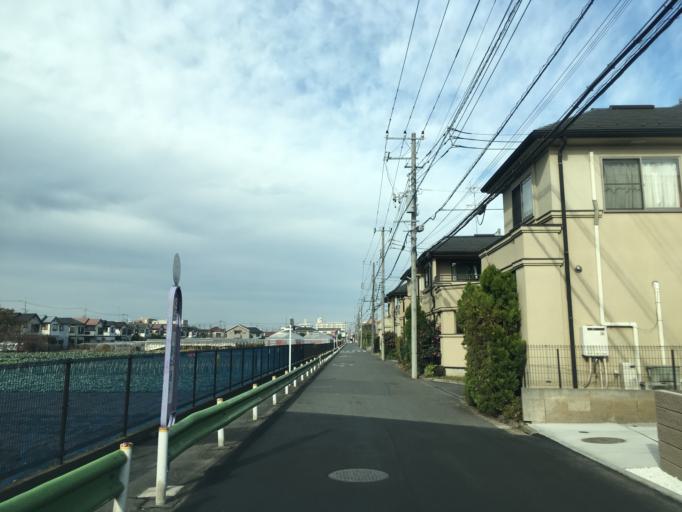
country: JP
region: Tokyo
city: Tanashicho
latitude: 35.7328
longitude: 139.5063
